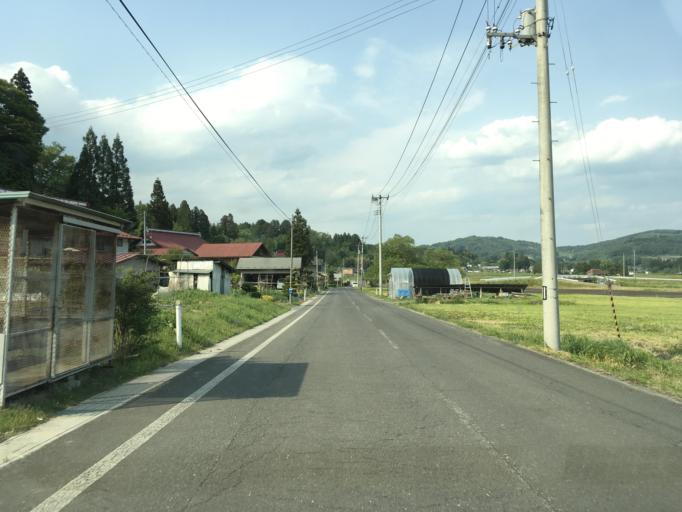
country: JP
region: Iwate
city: Ichinoseki
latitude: 38.9480
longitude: 141.3488
